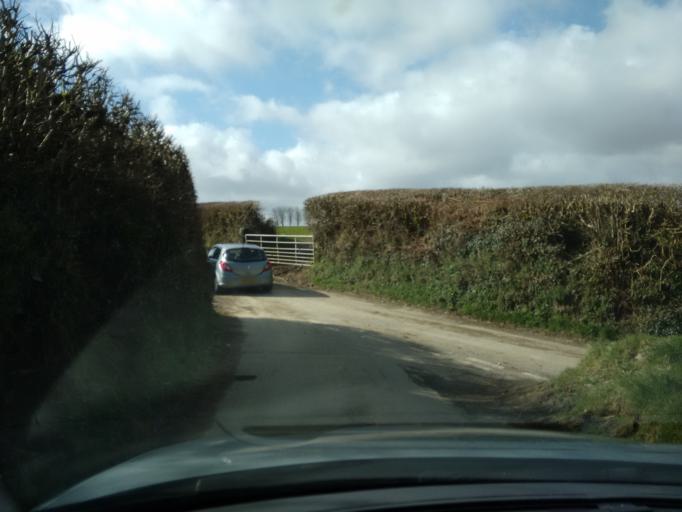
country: GB
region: England
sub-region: Cornwall
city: South Hill
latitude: 50.5543
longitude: -4.3859
